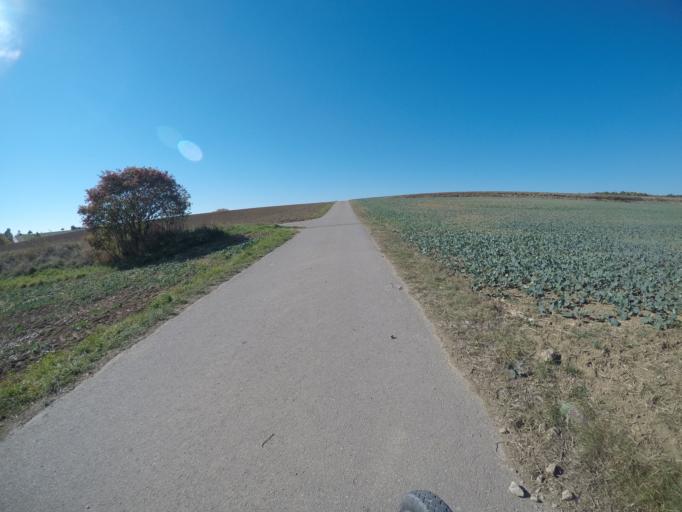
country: DE
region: Baden-Wuerttemberg
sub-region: Regierungsbezirk Stuttgart
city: Bondorf
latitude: 48.5372
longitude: 8.8765
